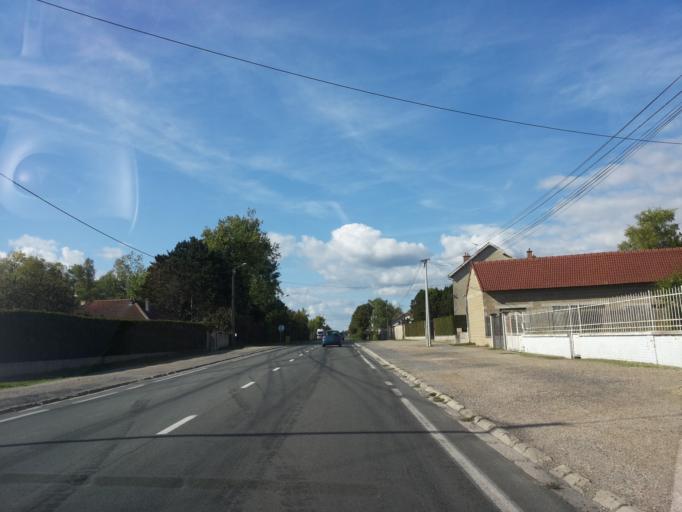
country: FR
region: Champagne-Ardenne
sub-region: Departement de la Marne
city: Cormicy
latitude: 49.4042
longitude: 3.8976
